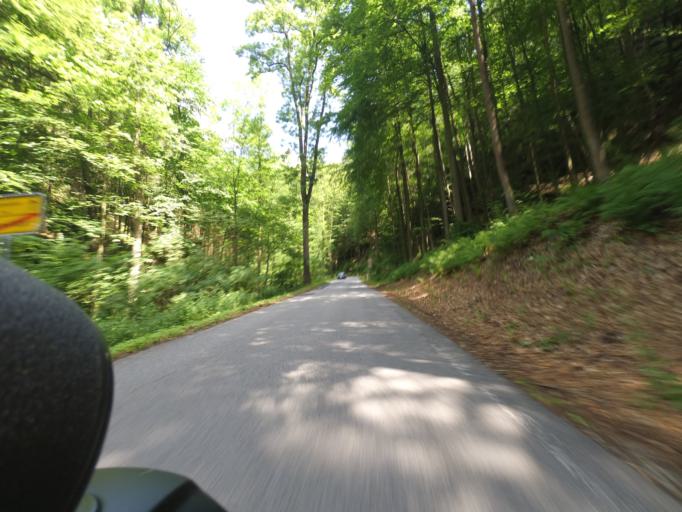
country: DE
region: Saxony
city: Porschdorf
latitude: 50.9460
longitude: 14.1369
